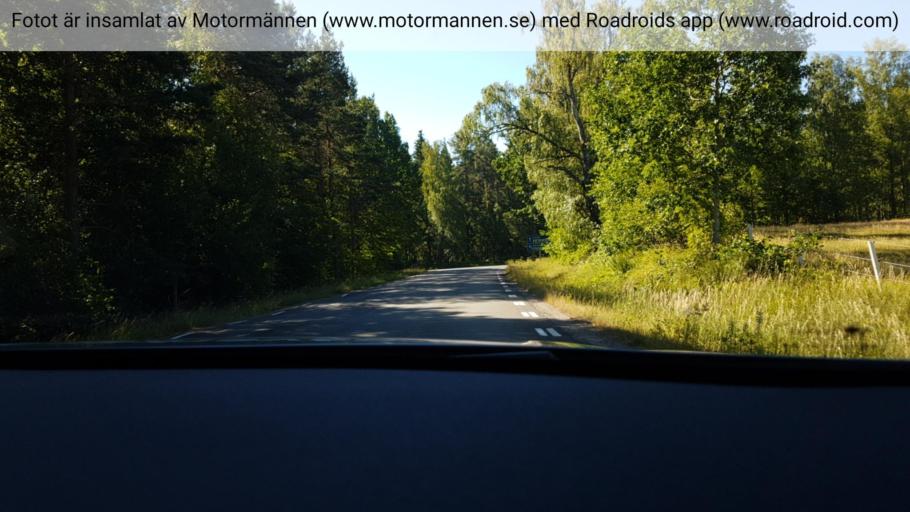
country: SE
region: Vaestra Goetaland
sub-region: Tidaholms Kommun
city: Tidaholm
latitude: 58.1043
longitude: 14.0765
